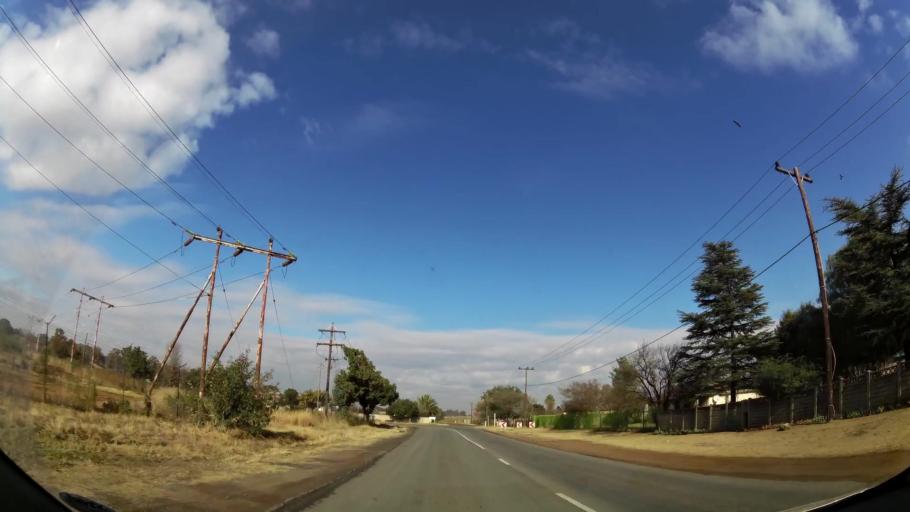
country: ZA
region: Gauteng
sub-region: Sedibeng District Municipality
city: Meyerton
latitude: -26.5195
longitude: 28.0466
